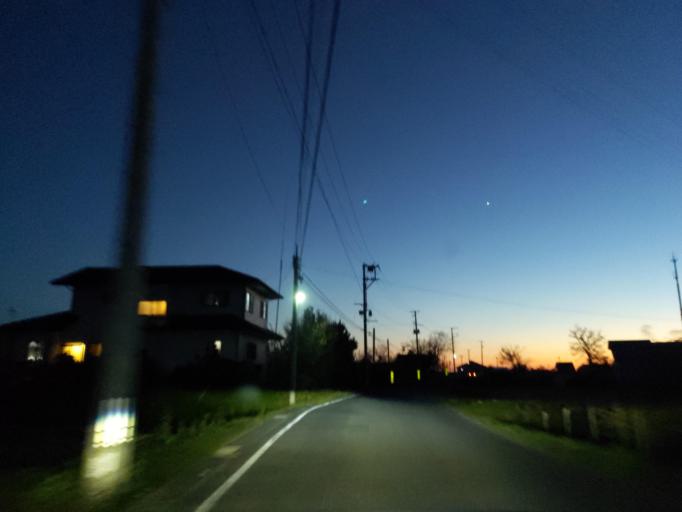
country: JP
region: Fukushima
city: Sukagawa
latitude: 37.3190
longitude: 140.3909
